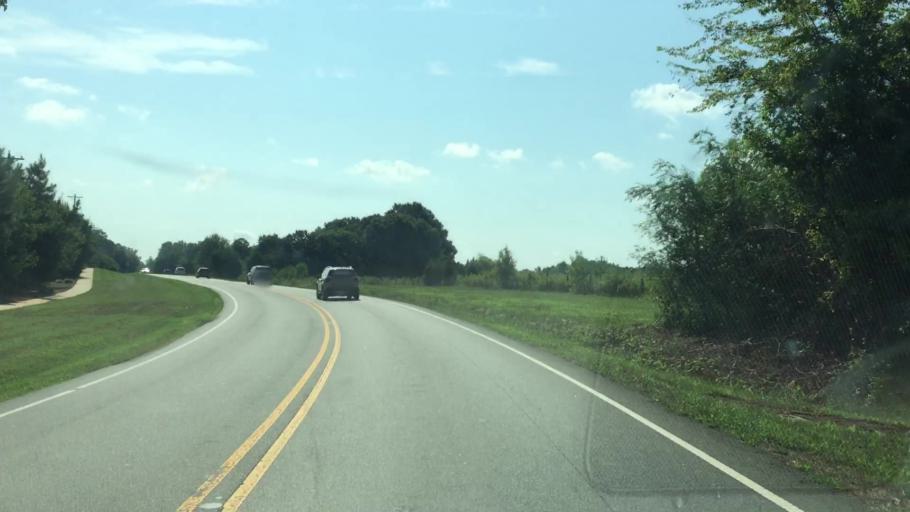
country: US
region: North Carolina
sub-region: Mecklenburg County
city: Mint Hill
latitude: 35.1726
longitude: -80.6175
